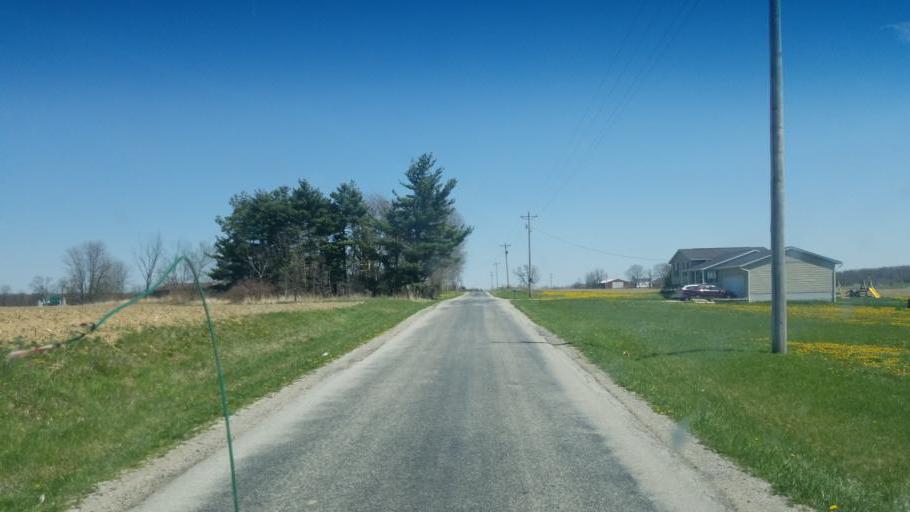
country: US
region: Ohio
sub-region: Huron County
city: Greenwich
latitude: 41.0476
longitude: -82.4916
